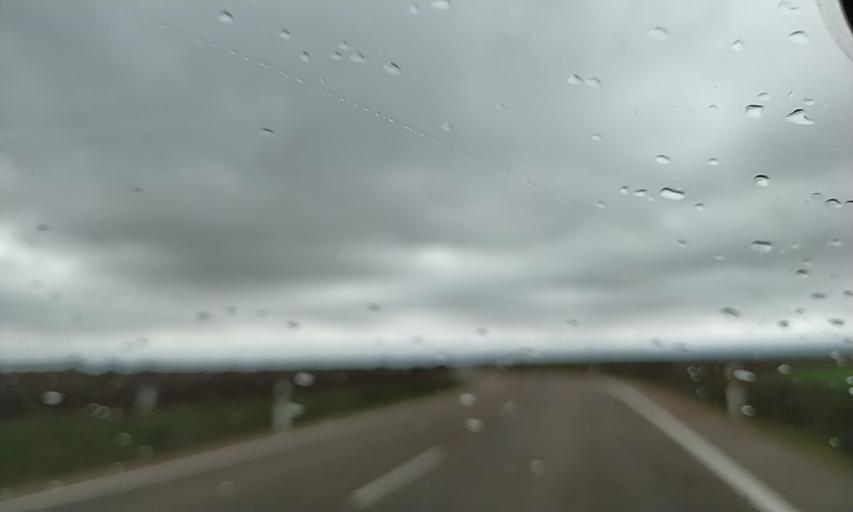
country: ES
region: Extremadura
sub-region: Provincia de Badajoz
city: Villar del Rey
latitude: 39.0530
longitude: -6.7972
